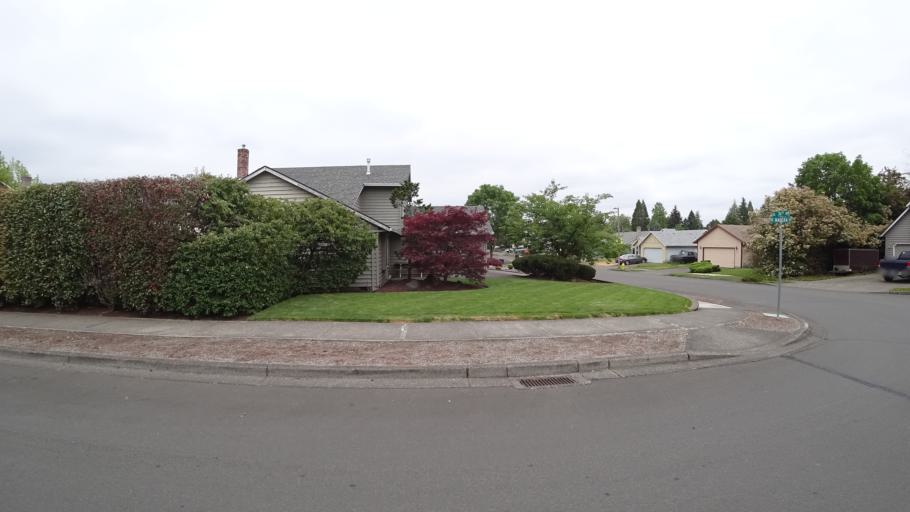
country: US
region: Oregon
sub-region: Washington County
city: Aloha
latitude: 45.5015
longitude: -122.9059
